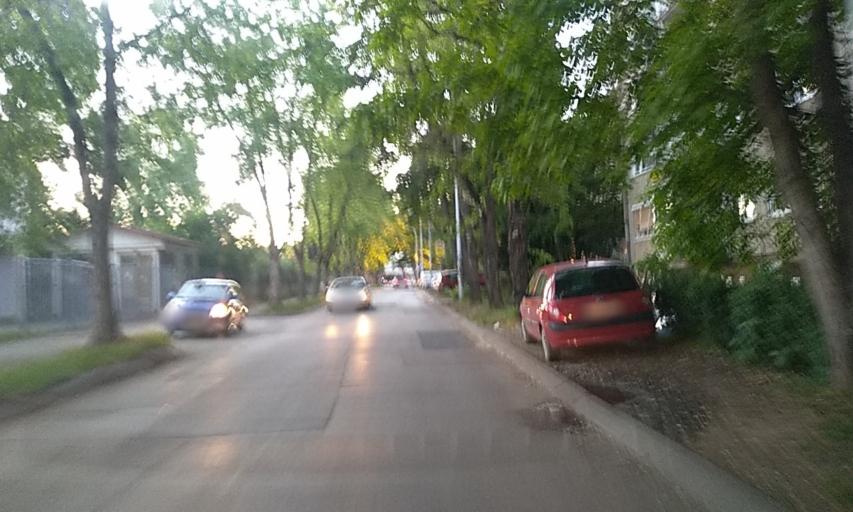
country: RS
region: Central Serbia
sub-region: Nisavski Okrug
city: Nis
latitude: 43.3213
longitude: 21.9215
